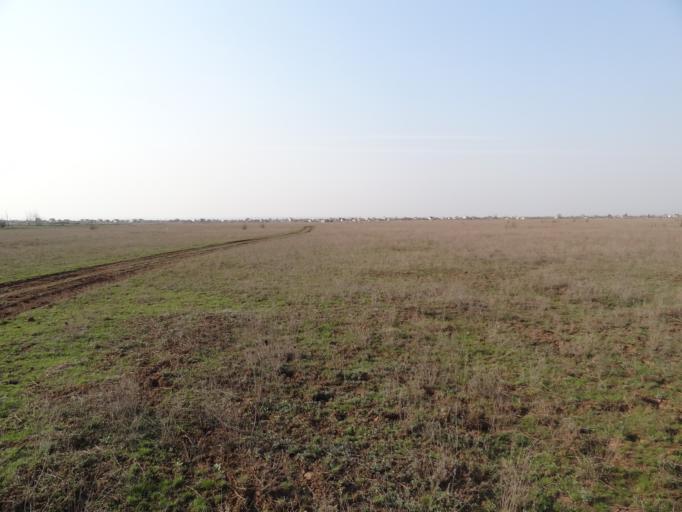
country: RU
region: Saratov
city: Privolzhskiy
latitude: 51.3273
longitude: 46.0177
